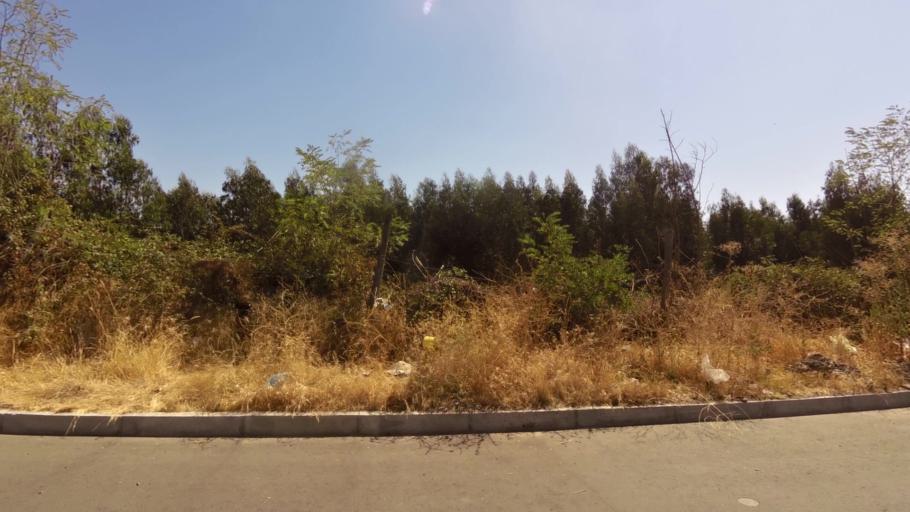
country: CL
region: Maule
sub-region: Provincia de Curico
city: Curico
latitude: -34.9600
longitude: -71.2334
